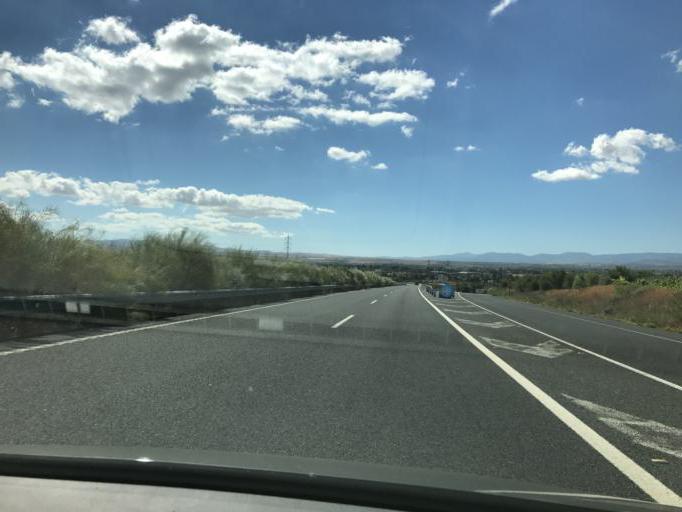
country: ES
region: Andalusia
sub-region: Provincia de Granada
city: Baza
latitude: 37.5081
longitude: -2.7723
